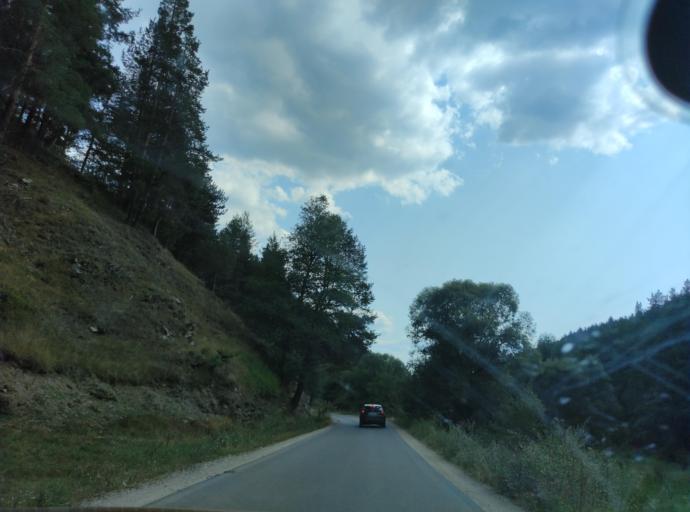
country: BG
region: Blagoevgrad
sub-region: Obshtina Belitsa
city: Belitsa
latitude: 41.9632
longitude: 23.5553
